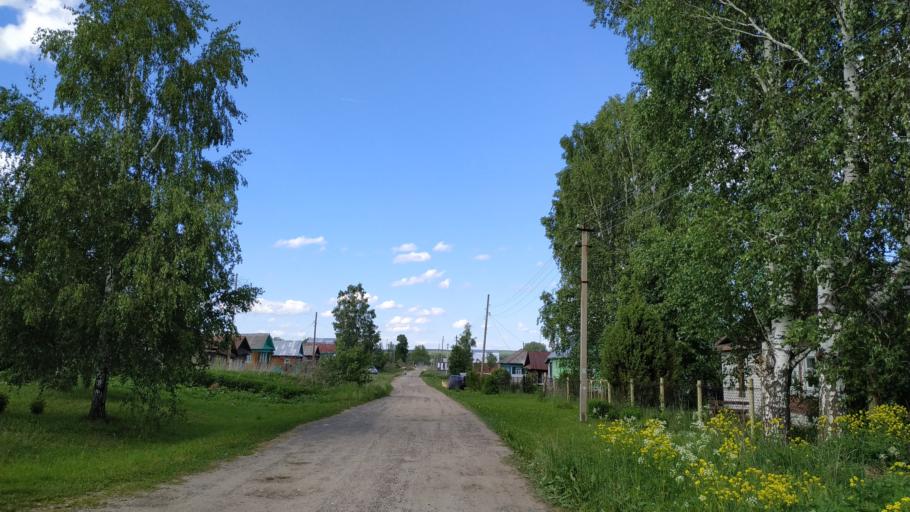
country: RU
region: Nizjnij Novgorod
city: Bogorodsk
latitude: 55.8838
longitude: 43.5565
